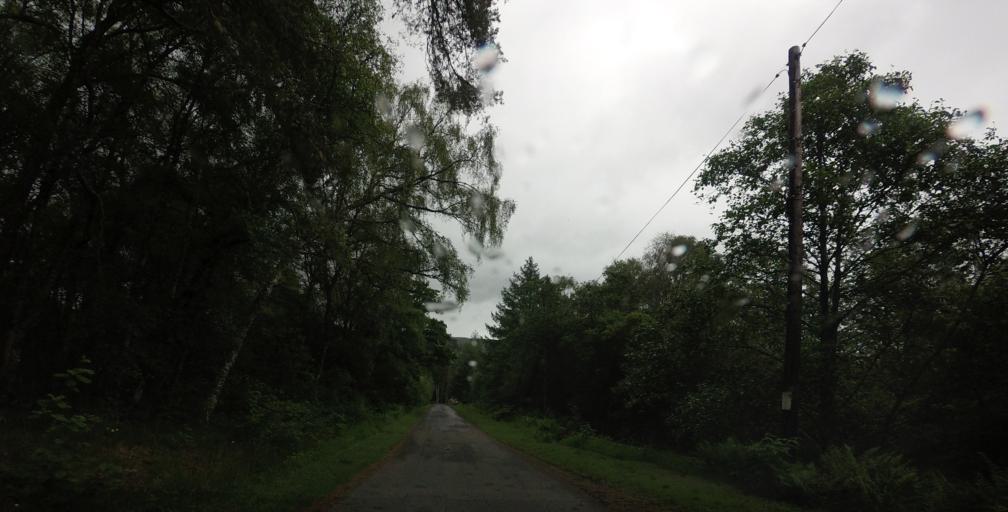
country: GB
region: Scotland
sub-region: Highland
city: Fort William
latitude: 56.8562
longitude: -5.2504
